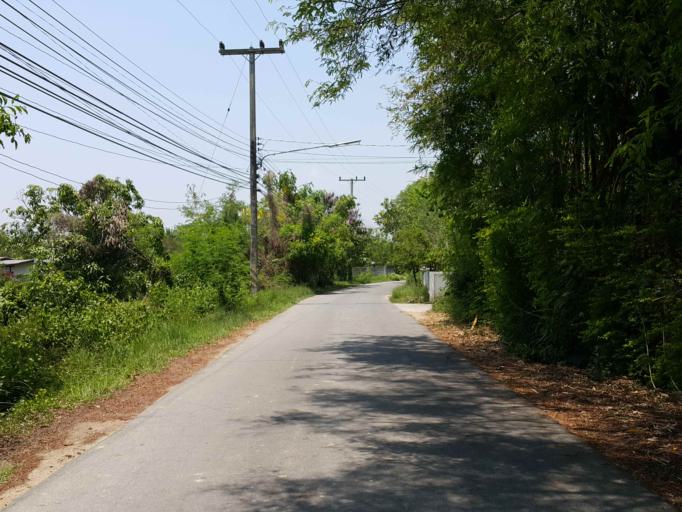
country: TH
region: Chiang Mai
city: San Sai
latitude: 18.8316
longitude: 99.1001
